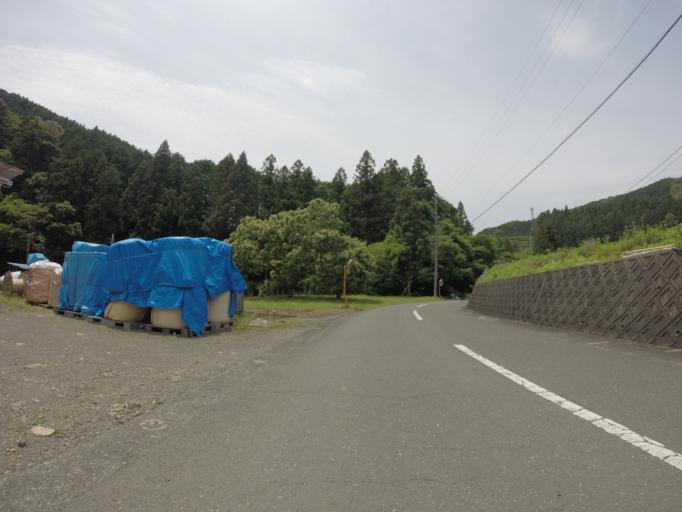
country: JP
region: Shizuoka
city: Shizuoka-shi
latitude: 35.0421
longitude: 138.2970
